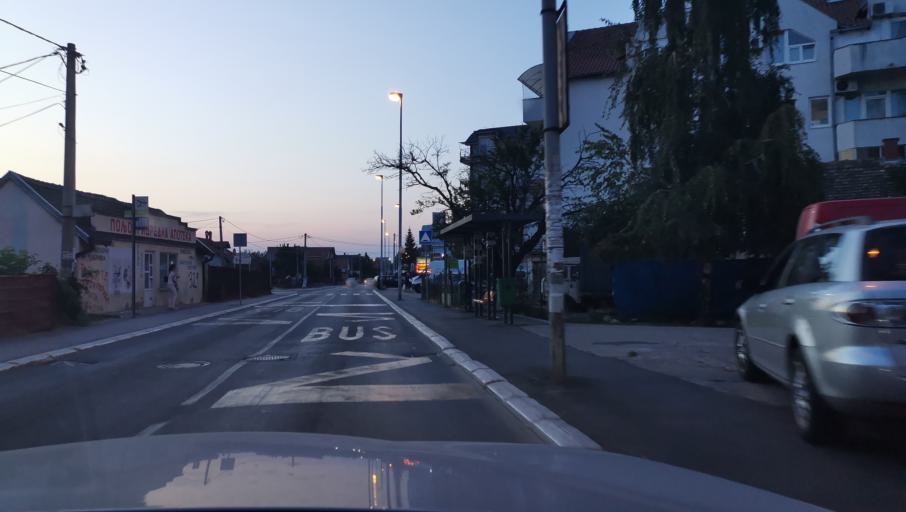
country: RS
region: Central Serbia
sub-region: Belgrade
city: Obrenovac
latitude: 44.6607
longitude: 20.2035
